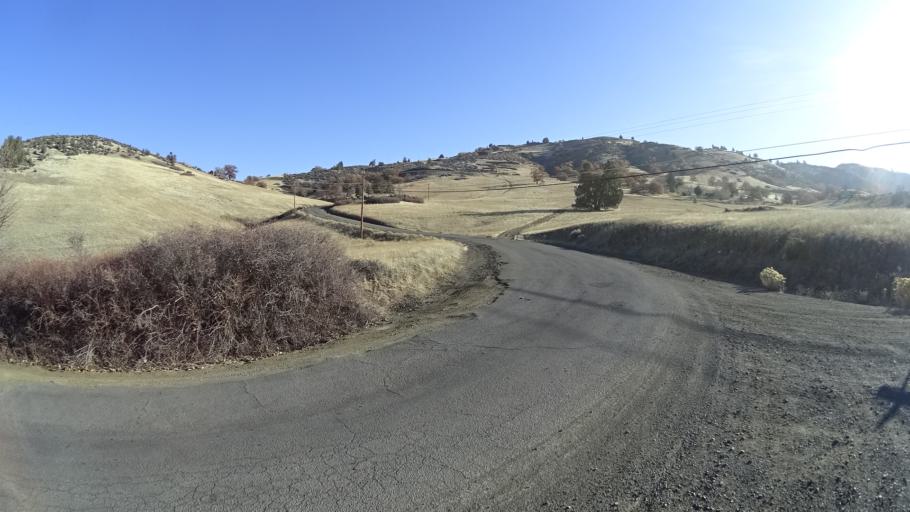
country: US
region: California
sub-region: Siskiyou County
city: Montague
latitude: 41.8881
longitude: -122.4791
